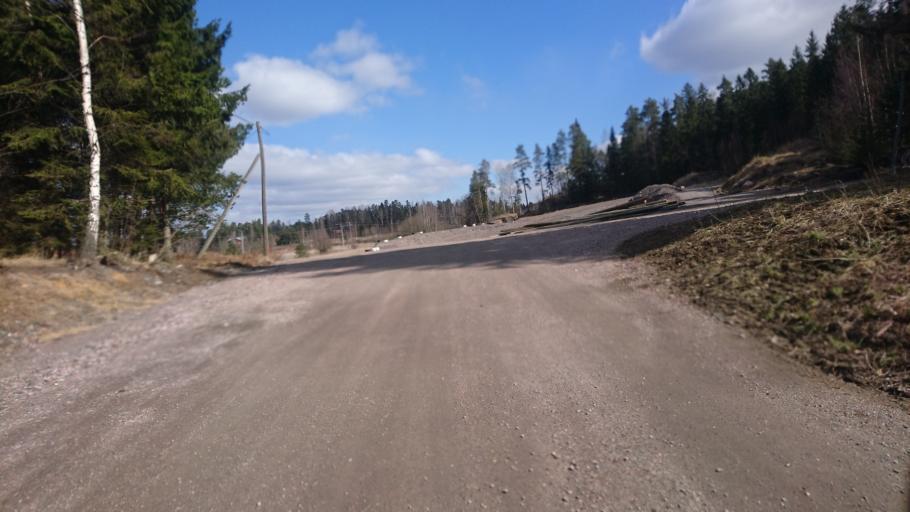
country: FI
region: Uusimaa
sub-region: Helsinki
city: Kauniainen
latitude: 60.1967
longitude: 24.7338
